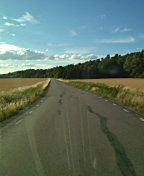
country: SE
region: Uppsala
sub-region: Habo Kommun
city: Balsta
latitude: 59.6738
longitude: 17.5422
